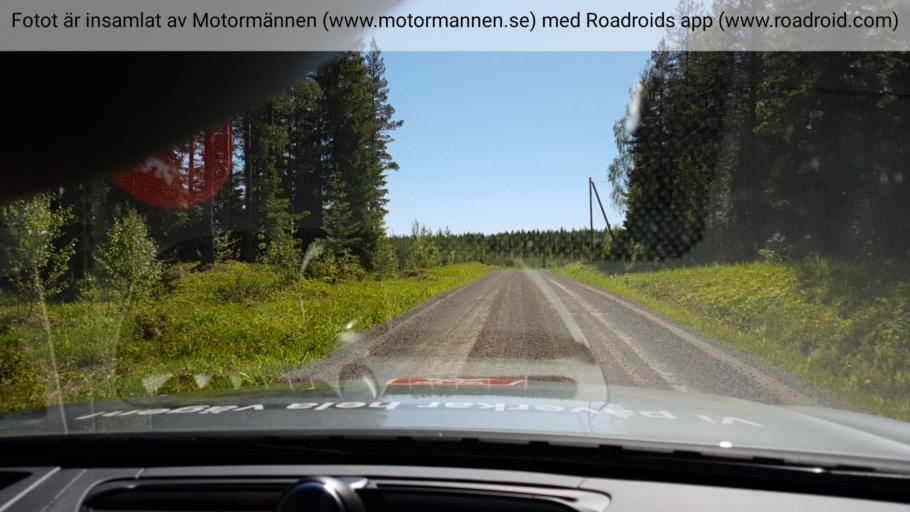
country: SE
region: Jaemtland
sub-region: OEstersunds Kommun
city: Brunflo
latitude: 62.9825
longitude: 14.7079
